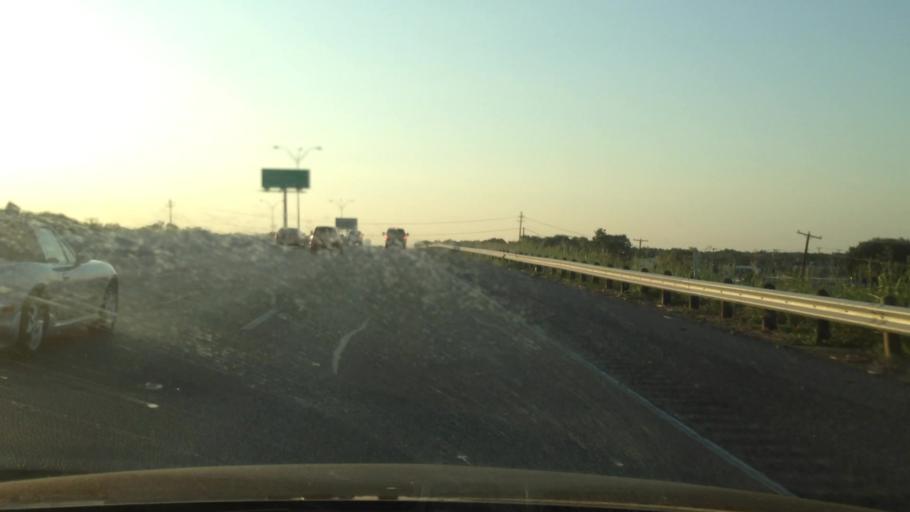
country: US
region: Texas
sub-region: Tarrant County
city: Forest Hill
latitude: 32.6988
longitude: -97.2614
